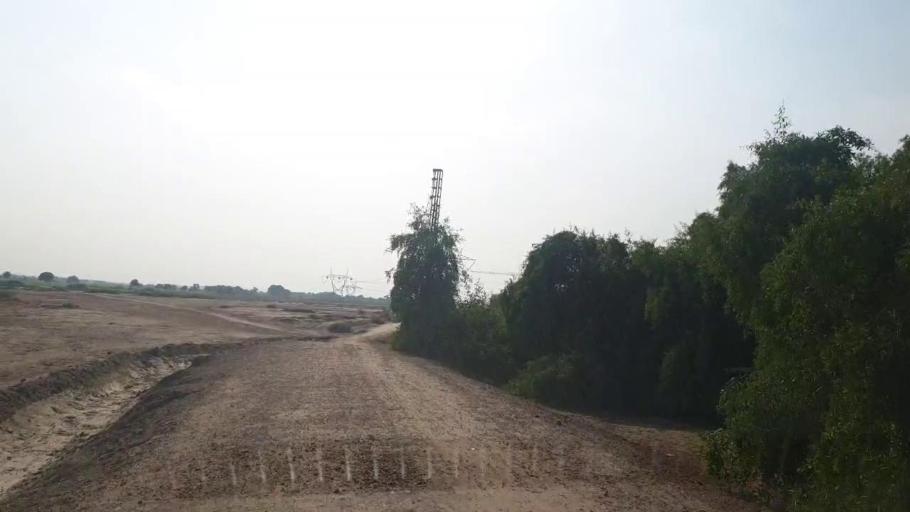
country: PK
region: Sindh
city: Hyderabad
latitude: 25.4667
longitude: 68.3766
